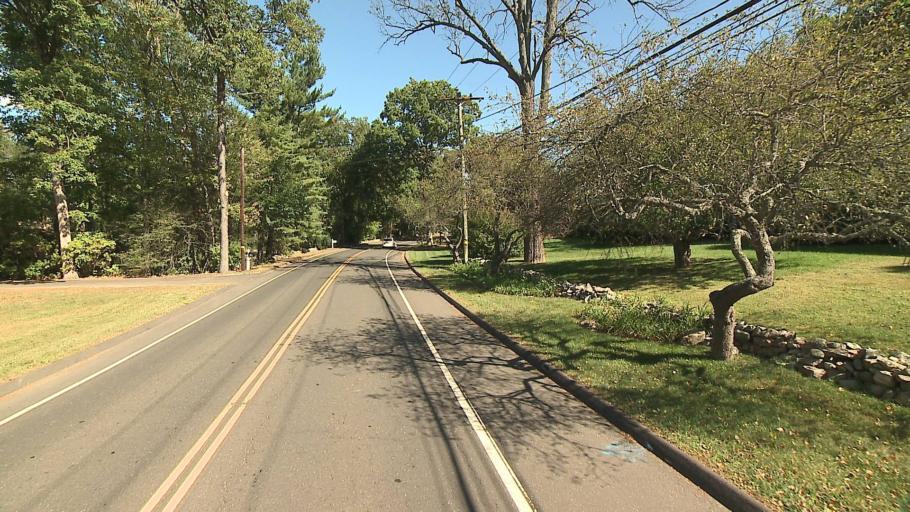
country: US
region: Connecticut
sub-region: Fairfield County
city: Darien
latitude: 41.1005
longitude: -73.5101
